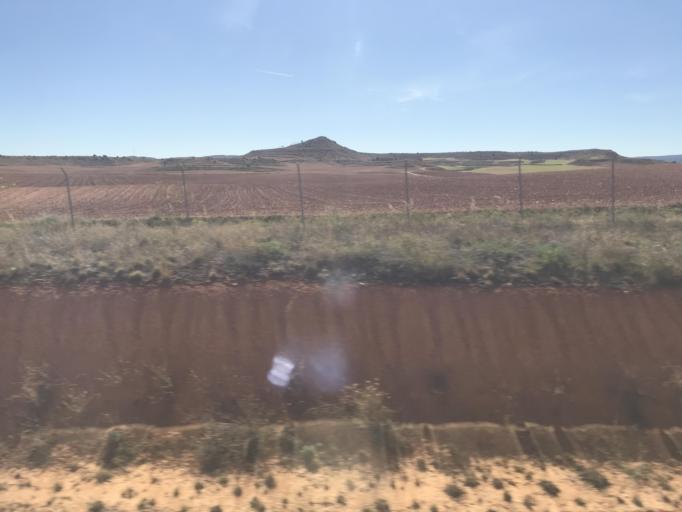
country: ES
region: Aragon
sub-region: Provincia de Zaragoza
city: Alconchel de Ariza
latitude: 41.2203
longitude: -2.1032
